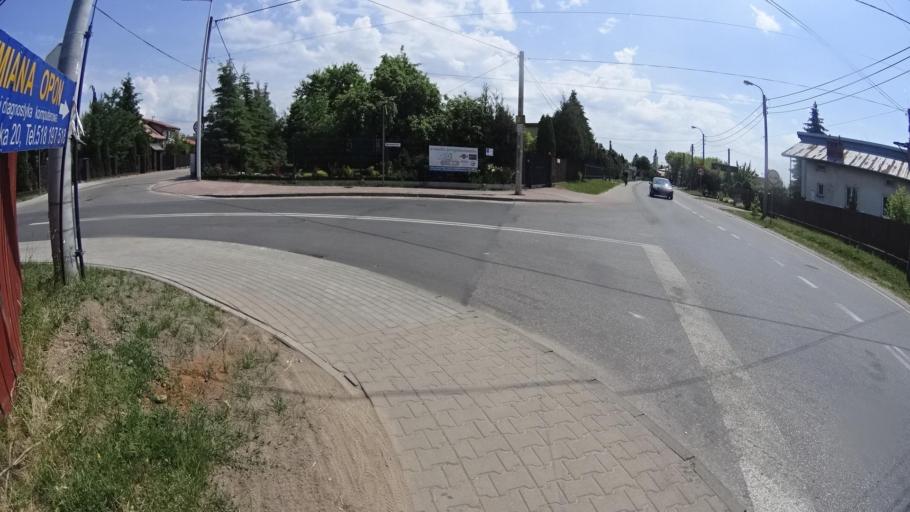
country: PL
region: Masovian Voivodeship
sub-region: Powiat warszawski zachodni
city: Stare Babice
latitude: 52.2570
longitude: 20.8379
